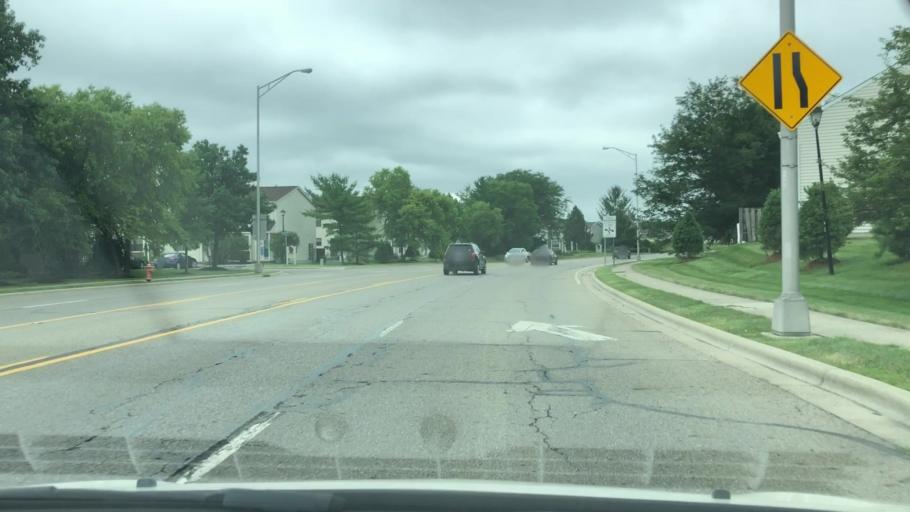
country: US
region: Ohio
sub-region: Franklin County
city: Worthington
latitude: 40.1335
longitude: -82.9914
